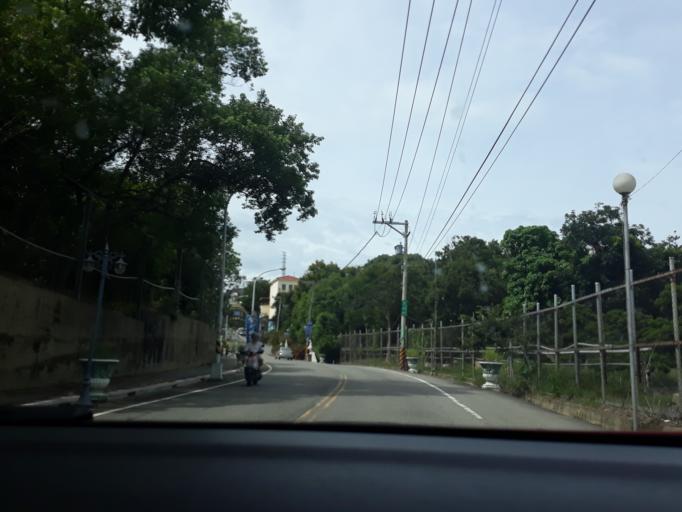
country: TW
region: Taiwan
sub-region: Miaoli
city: Miaoli
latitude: 24.5532
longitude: 120.8105
